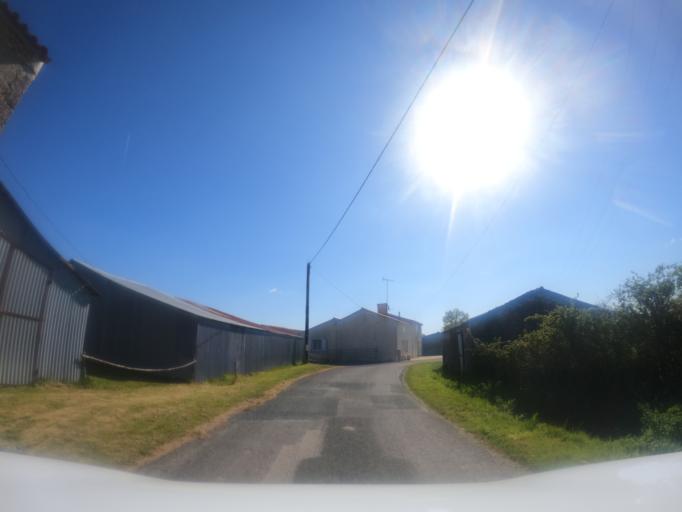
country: FR
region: Pays de la Loire
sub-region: Departement de la Vendee
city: Le Champ-Saint-Pere
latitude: 46.5391
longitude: -1.3555
